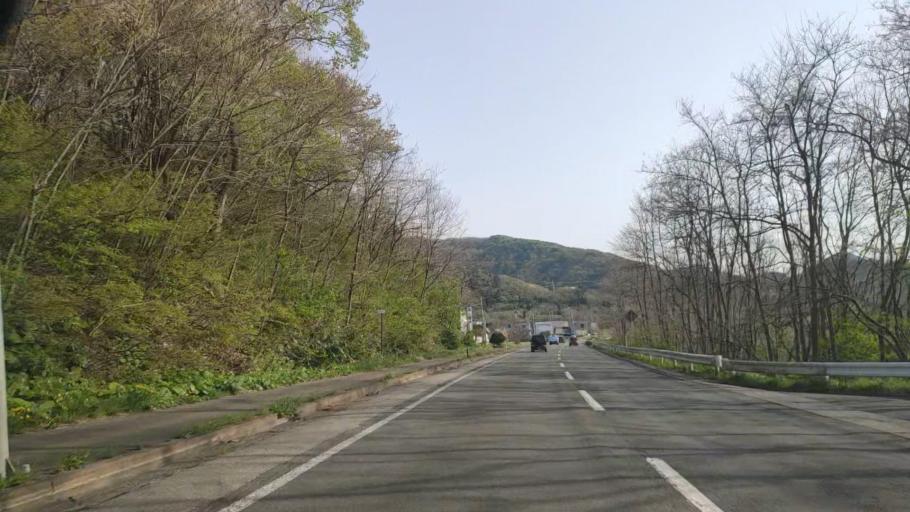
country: JP
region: Aomori
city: Aomori Shi
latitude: 40.8741
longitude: 140.8516
